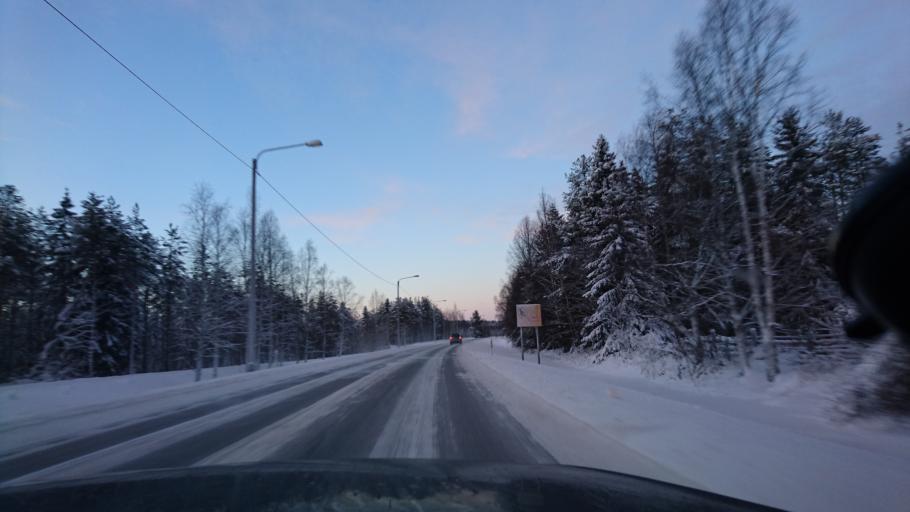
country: FI
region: Lapland
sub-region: Rovaniemi
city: Ranua
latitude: 65.9337
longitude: 26.4980
